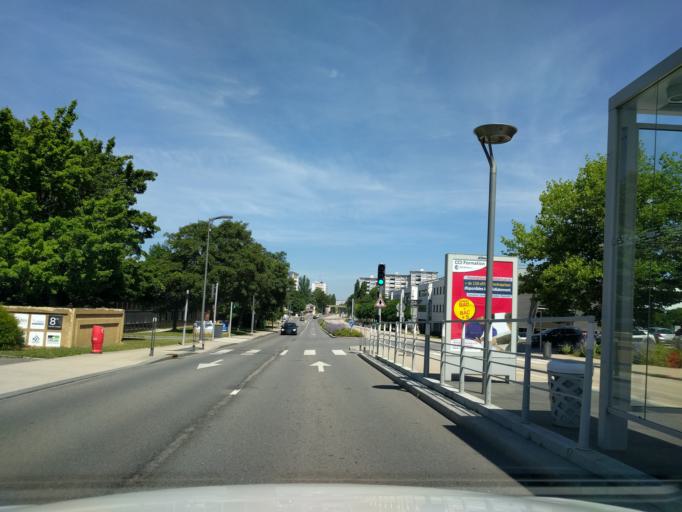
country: FR
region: Lorraine
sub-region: Departement de la Moselle
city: Peltre
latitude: 49.1051
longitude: 6.2232
